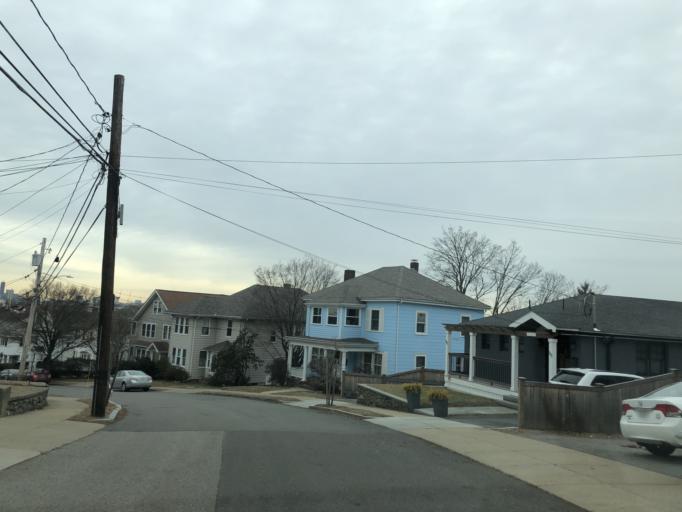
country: US
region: Massachusetts
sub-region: Middlesex County
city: Watertown
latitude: 42.3664
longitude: -71.1698
